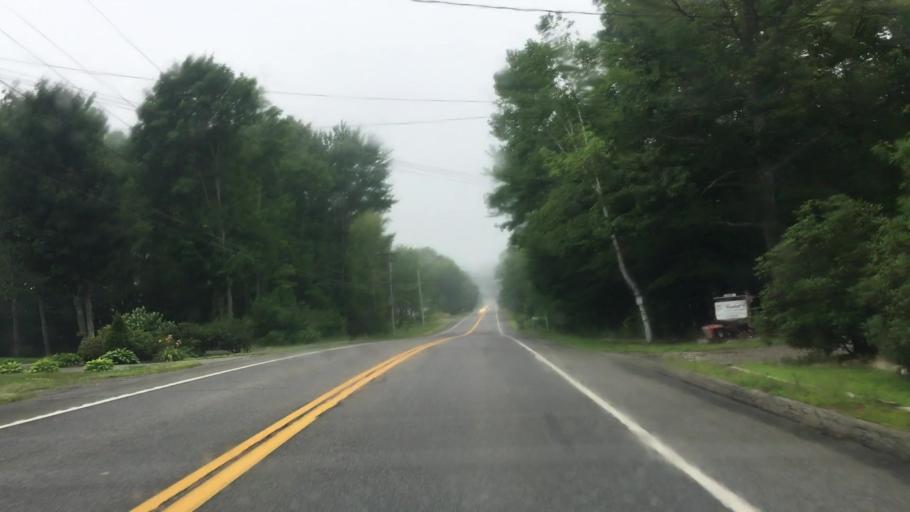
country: US
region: Maine
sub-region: Lincoln County
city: Wiscasset
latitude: 44.0497
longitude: -69.6805
